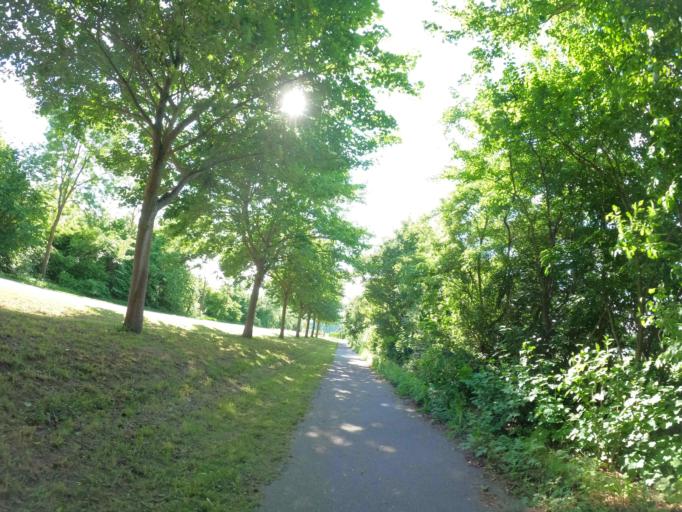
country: DE
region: Mecklenburg-Vorpommern
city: Kramerhof
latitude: 54.3406
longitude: 13.0459
